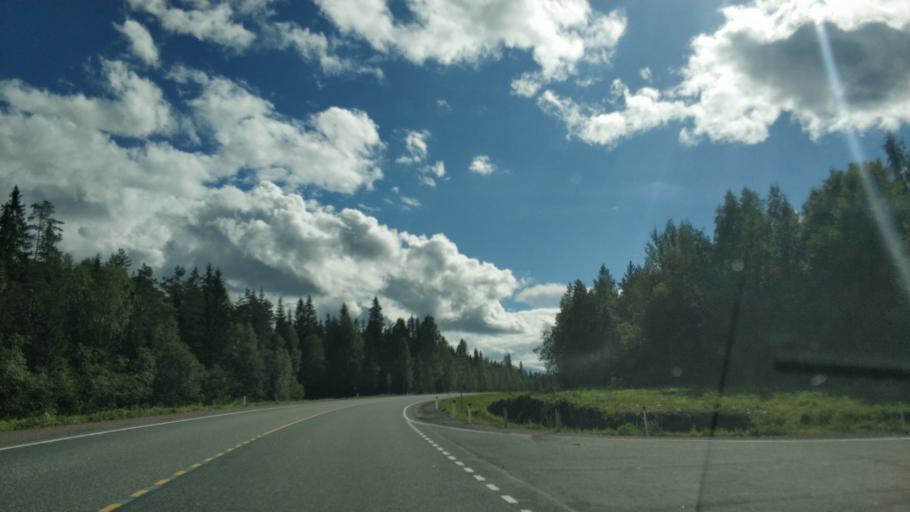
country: RU
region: Republic of Karelia
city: Ruskeala
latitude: 61.8682
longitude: 30.6535
